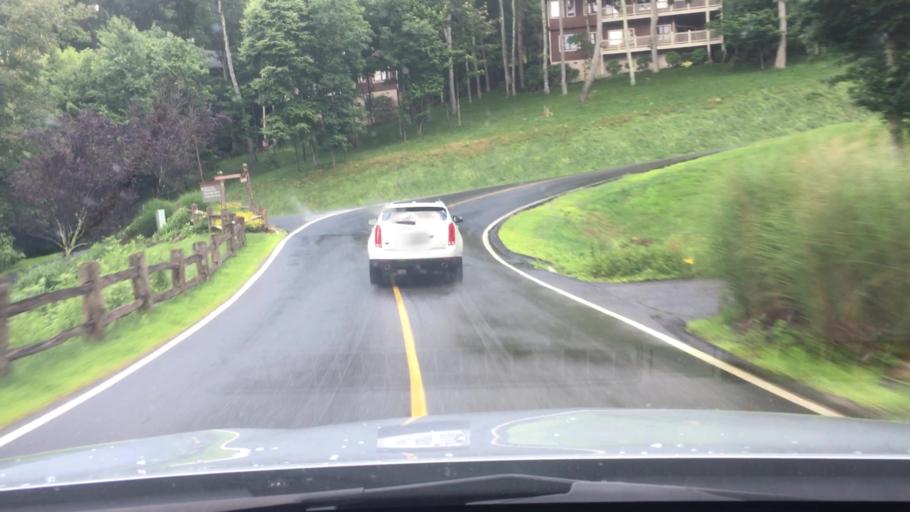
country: US
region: North Carolina
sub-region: Yancey County
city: Burnsville
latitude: 35.8741
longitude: -82.3447
